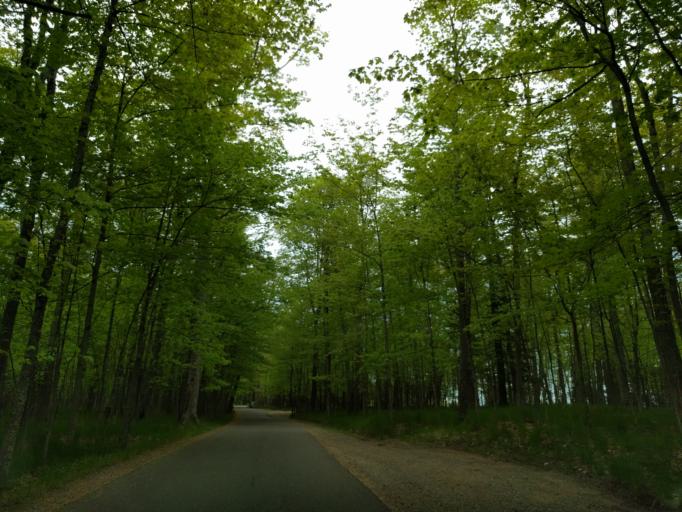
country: US
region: Michigan
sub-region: Marquette County
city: Marquette
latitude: 46.5836
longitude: -87.3802
